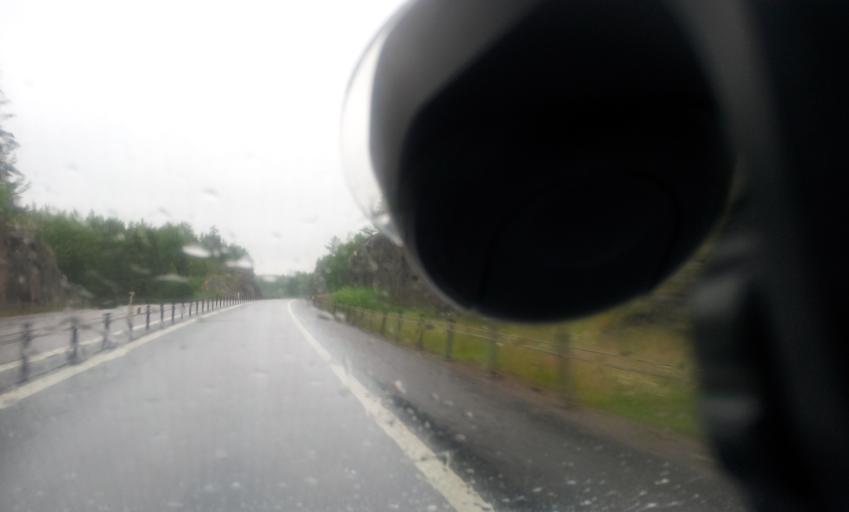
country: SE
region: OEstergoetland
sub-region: Valdemarsviks Kommun
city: Gusum
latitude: 58.3480
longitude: 16.4475
